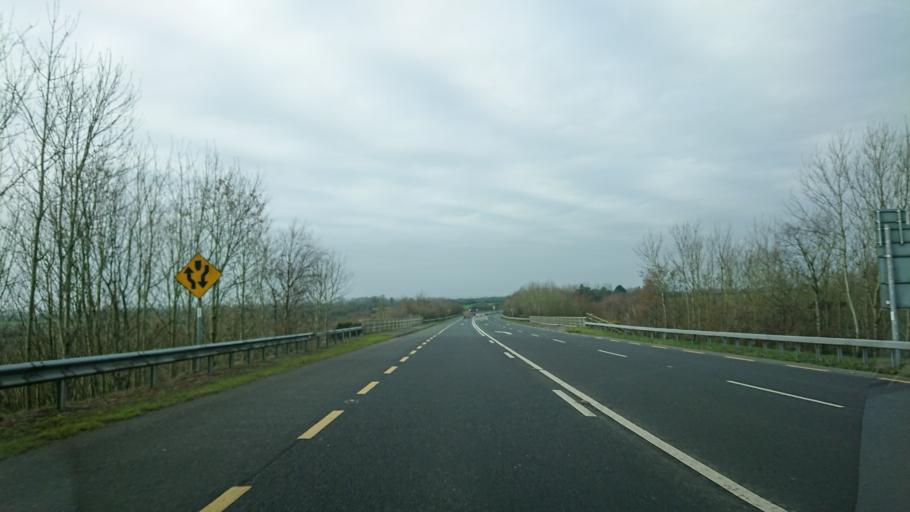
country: IE
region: Munster
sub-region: County Cork
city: Youghal
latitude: 51.9412
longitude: -7.8975
